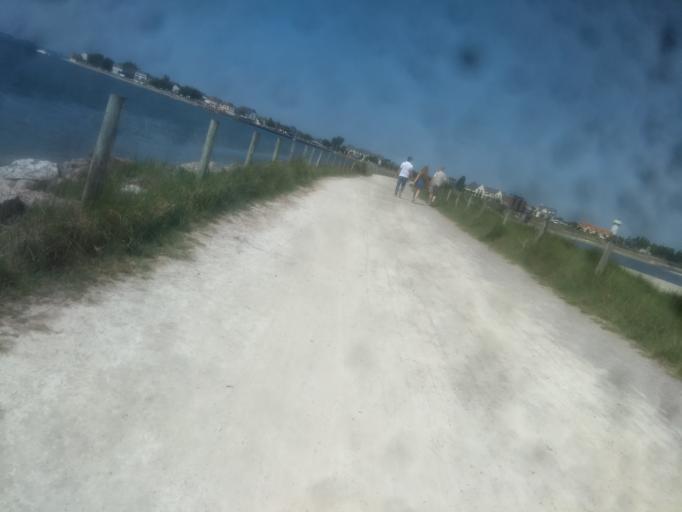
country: FR
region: Picardie
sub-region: Departement de la Somme
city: Le Crotoy
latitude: 50.2134
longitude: 1.6368
